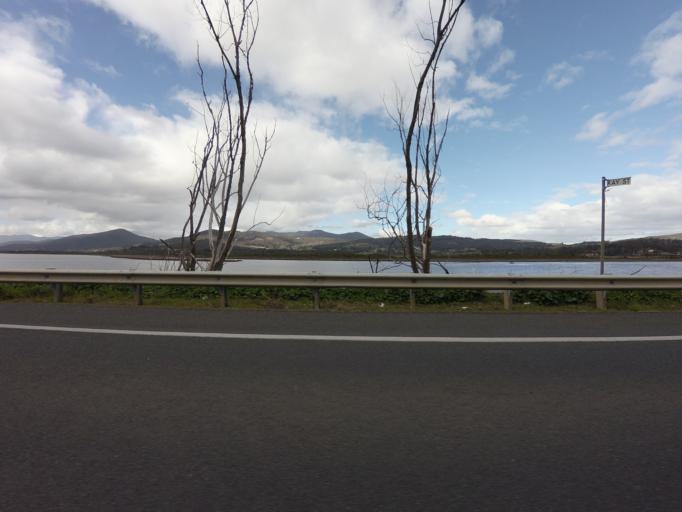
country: AU
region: Tasmania
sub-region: Huon Valley
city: Franklin
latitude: -43.1071
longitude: 147.0005
